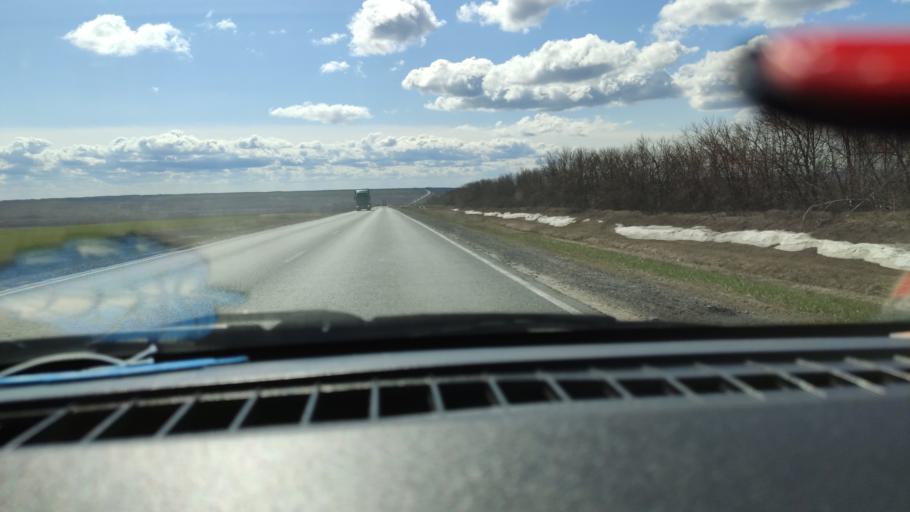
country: RU
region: Saratov
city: Dukhovnitskoye
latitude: 52.7558
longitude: 48.2449
